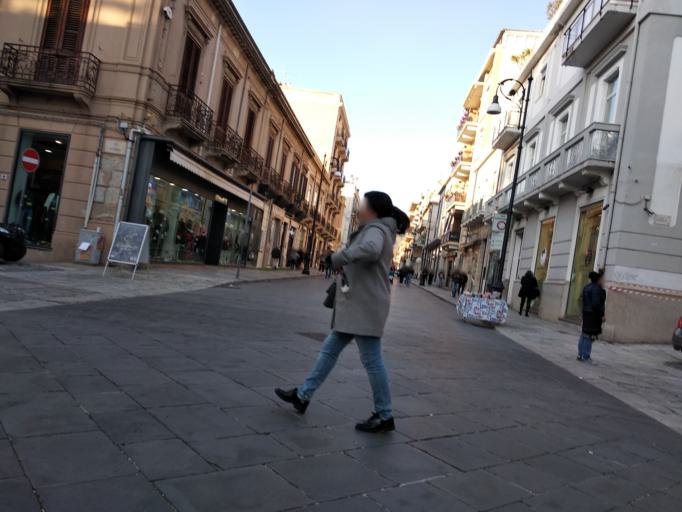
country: IT
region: Calabria
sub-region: Provincia di Reggio Calabria
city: Reggio Calabria
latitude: 38.1123
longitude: 15.6487
